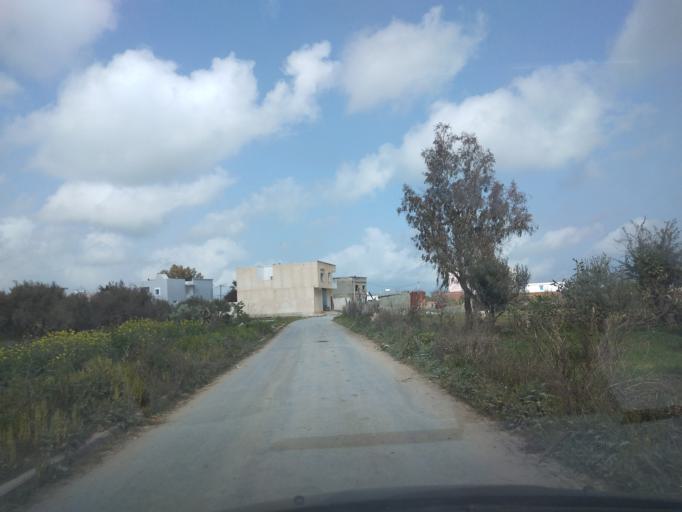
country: TN
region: Ariana
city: Qal'at al Andalus
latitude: 37.0663
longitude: 10.1257
